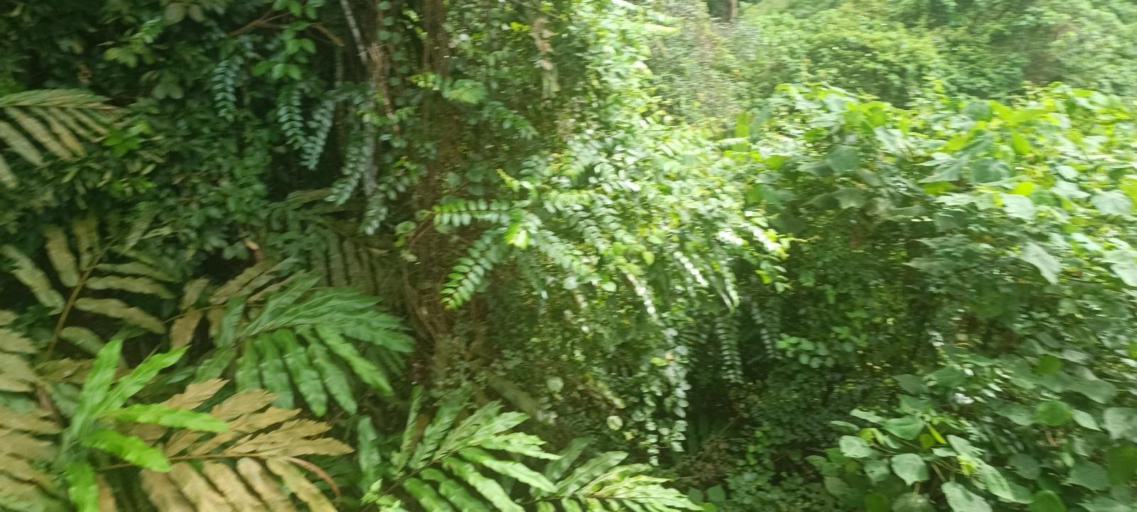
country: MY
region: Penang
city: Bukit Mertajam
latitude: 5.3742
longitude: 100.4955
